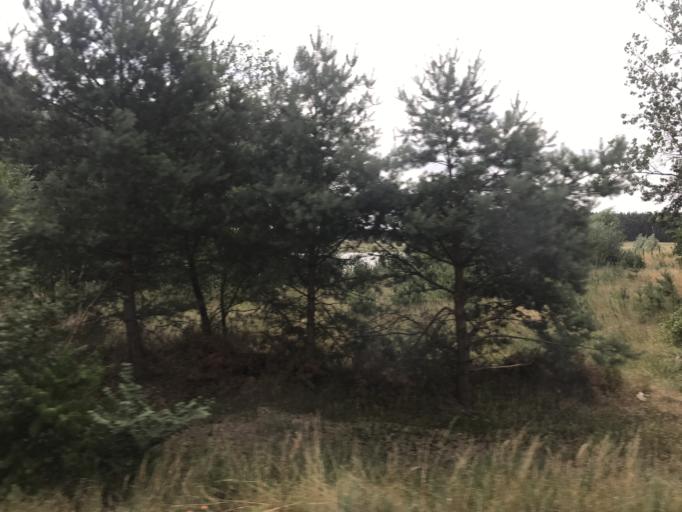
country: PL
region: Greater Poland Voivodeship
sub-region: Powiat gnieznienski
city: Trzemeszno
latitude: 52.5481
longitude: 17.7468
